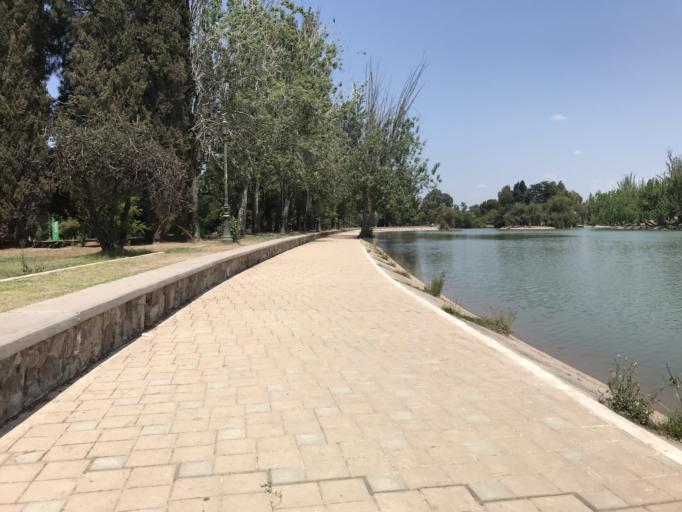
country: AR
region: Mendoza
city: Mendoza
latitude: -32.8941
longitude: -68.8652
